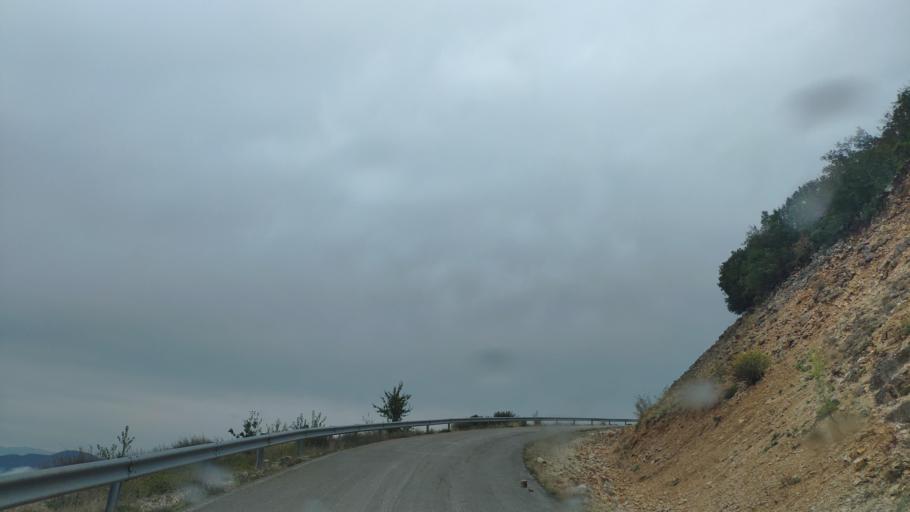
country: GR
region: Epirus
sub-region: Nomos Thesprotias
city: Paramythia
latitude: 39.4558
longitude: 20.6683
